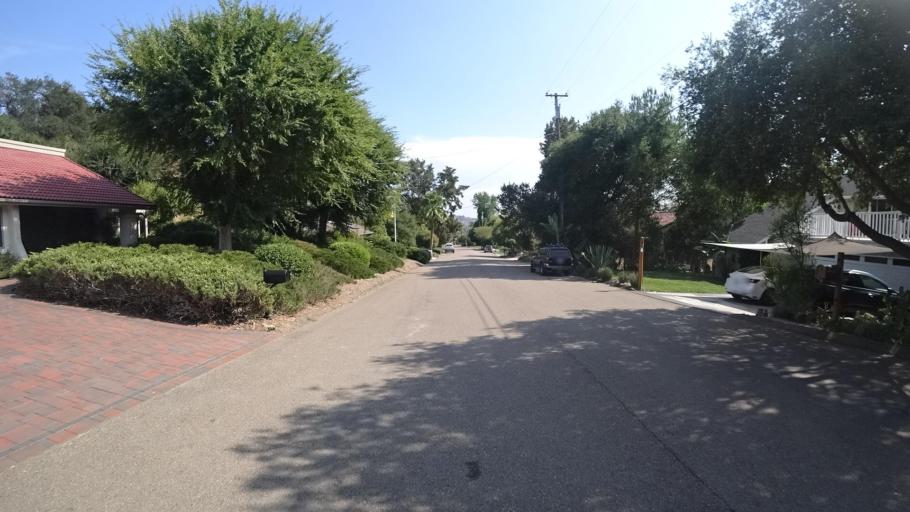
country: US
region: California
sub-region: San Diego County
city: Escondido
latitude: 33.0884
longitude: -117.0626
